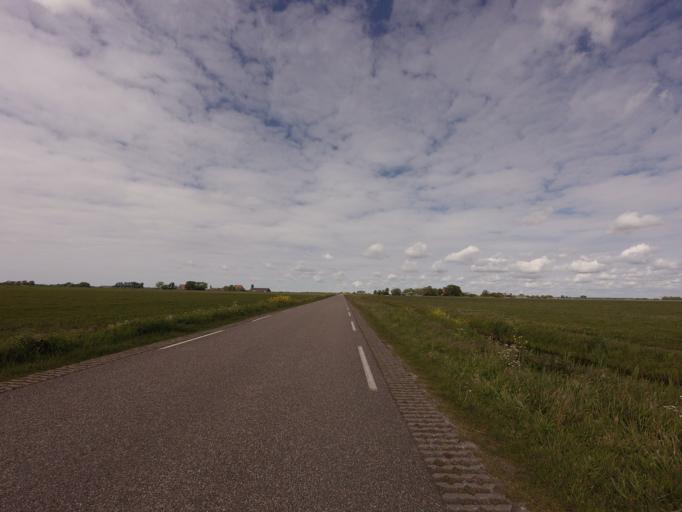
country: NL
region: Friesland
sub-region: Sudwest Fryslan
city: Bolsward
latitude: 53.0074
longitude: 5.5504
